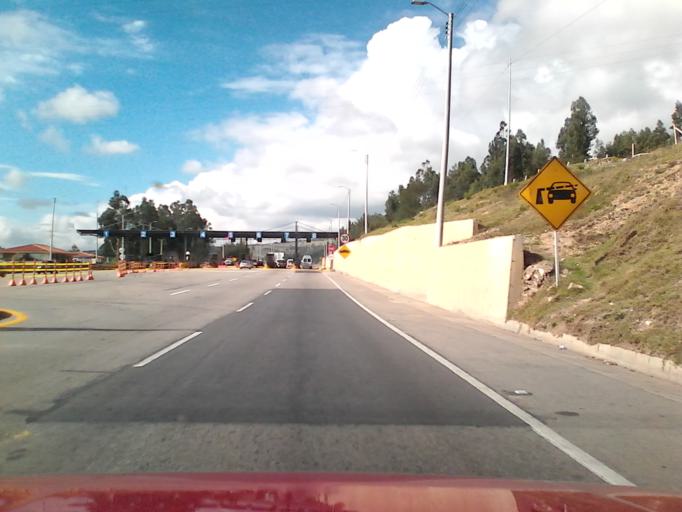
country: CO
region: Boyaca
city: Combita
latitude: 5.6581
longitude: -73.2775
